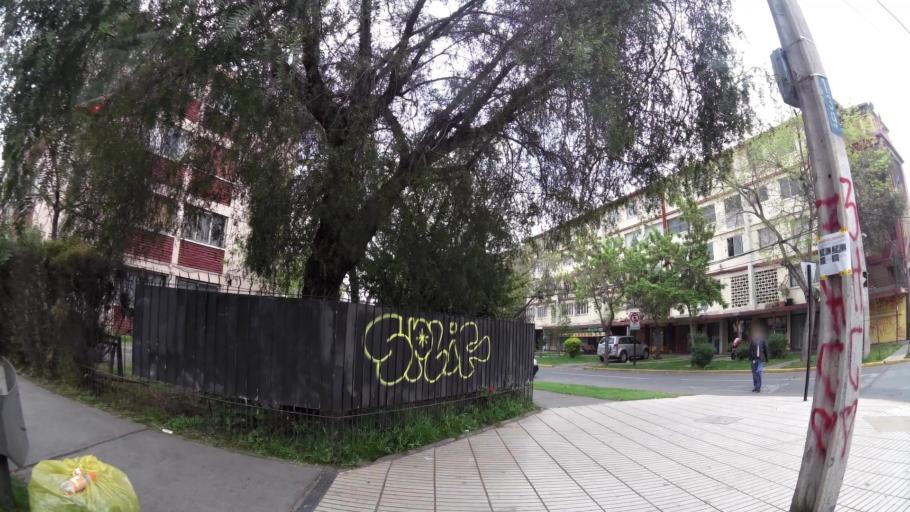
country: CL
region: Santiago Metropolitan
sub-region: Provincia de Santiago
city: Villa Presidente Frei, Nunoa, Santiago, Chile
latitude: -33.4646
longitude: -70.6014
